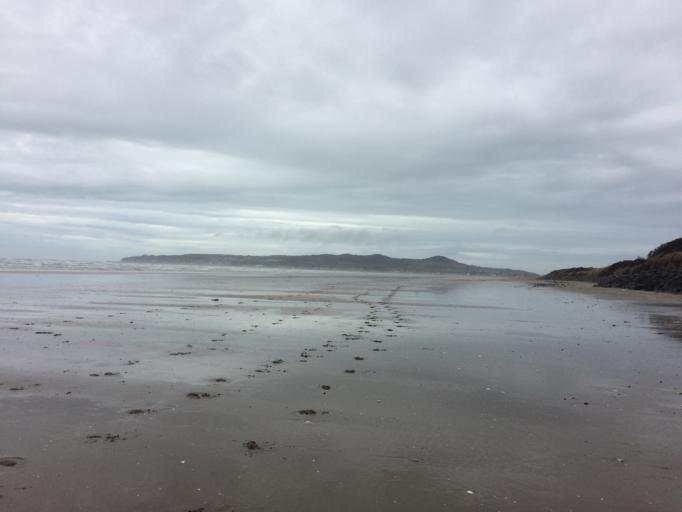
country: IE
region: Leinster
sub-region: Fingal County
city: Baldoyle
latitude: 53.4129
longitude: -6.1171
